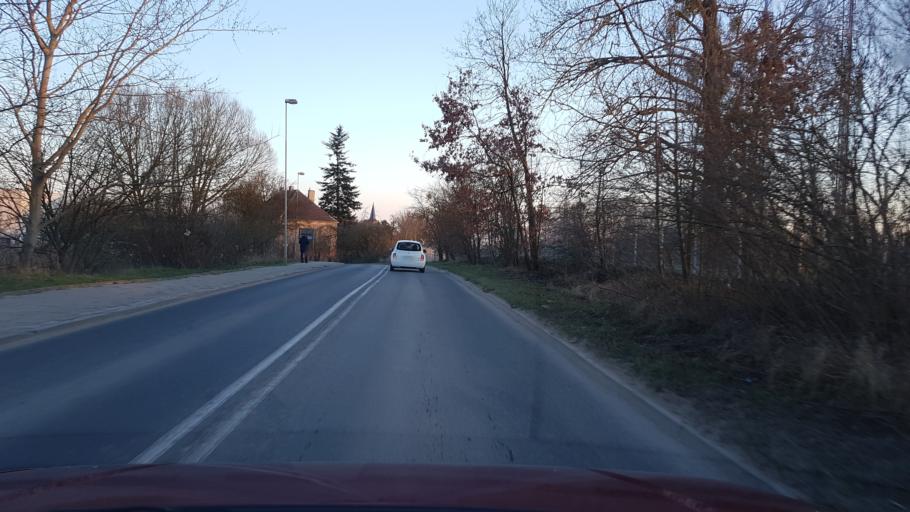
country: PL
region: West Pomeranian Voivodeship
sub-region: Szczecin
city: Szczecin
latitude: 53.4763
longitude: 14.5448
